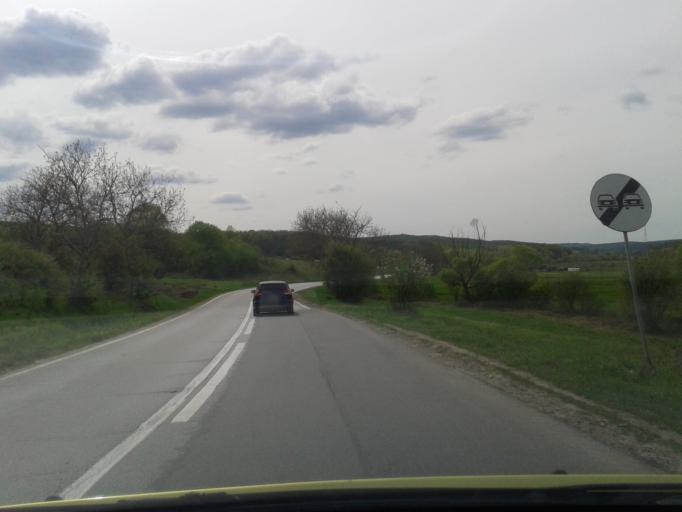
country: RO
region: Hunedoara
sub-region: Comuna Dobra
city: Dobra
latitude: 45.9186
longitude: 22.5559
